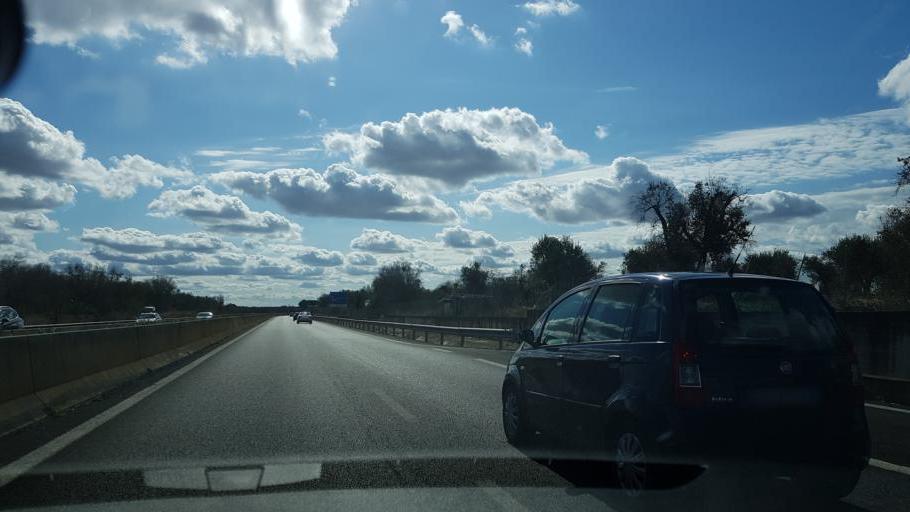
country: IT
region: Apulia
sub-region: Provincia di Lecce
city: Squinzano
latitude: 40.4476
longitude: 18.0711
